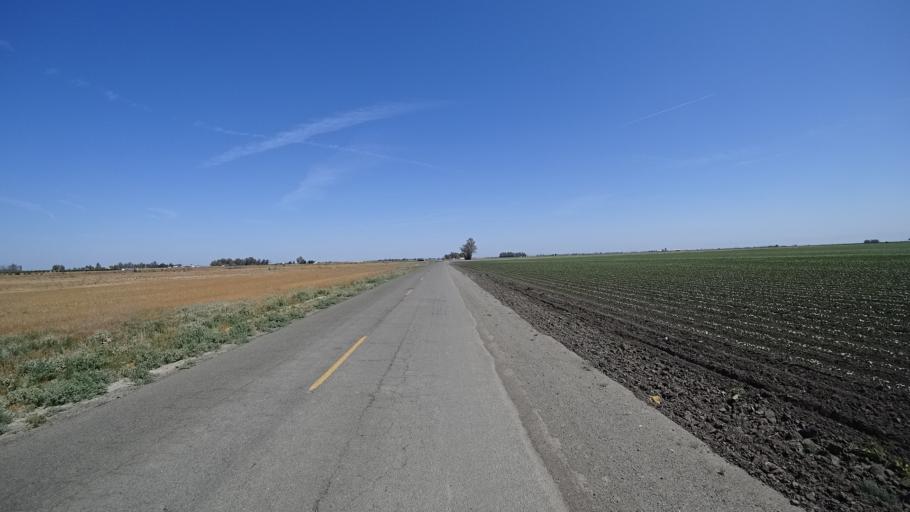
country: US
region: California
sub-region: Kings County
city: Stratford
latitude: 36.1865
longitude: -119.7803
